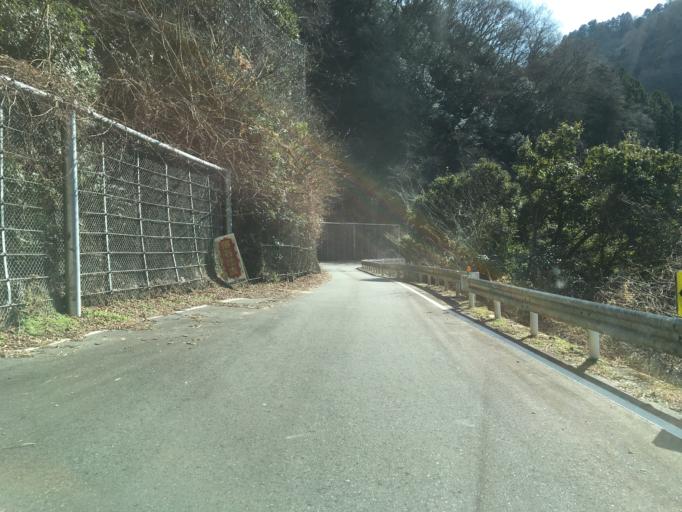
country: JP
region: Ibaraki
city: Kitaibaraki
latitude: 36.7823
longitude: 140.6780
